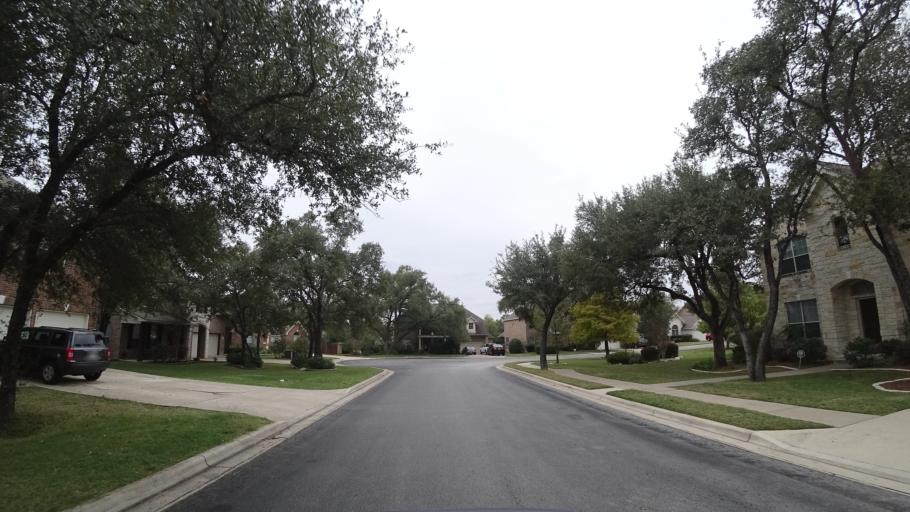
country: US
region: Texas
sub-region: Travis County
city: Shady Hollow
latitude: 30.1858
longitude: -97.9056
